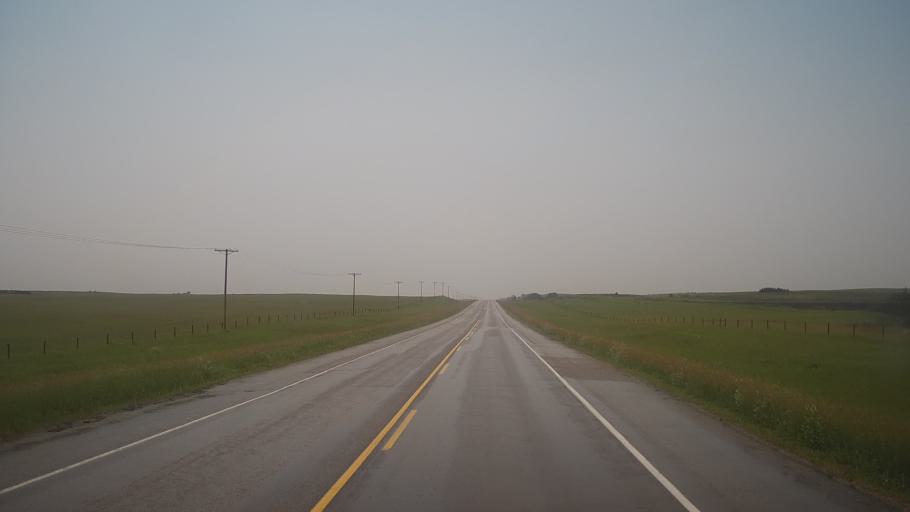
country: CA
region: Saskatchewan
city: Biggar
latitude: 52.0811
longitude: -108.0328
